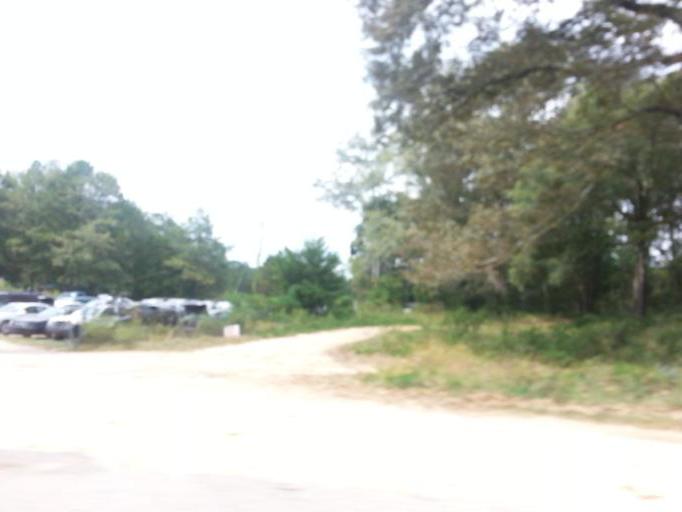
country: US
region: Alabama
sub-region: Bibb County
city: North Bibb
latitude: 33.1662
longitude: -87.1528
